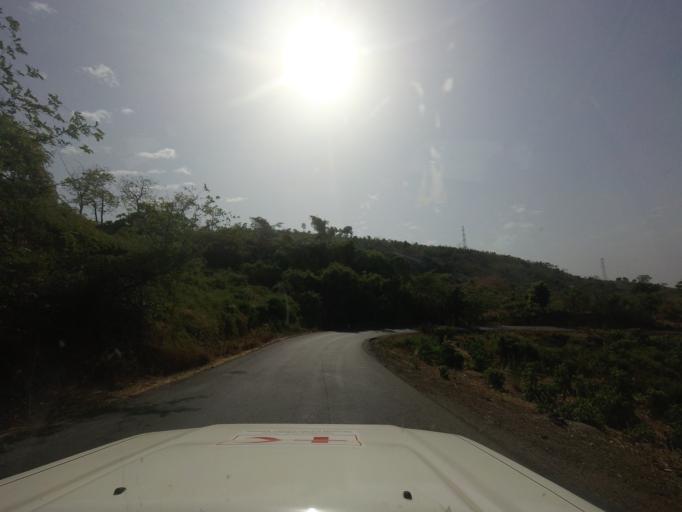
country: GN
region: Mamou
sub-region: Mamou Prefecture
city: Mamou
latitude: 10.2232
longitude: -12.4615
